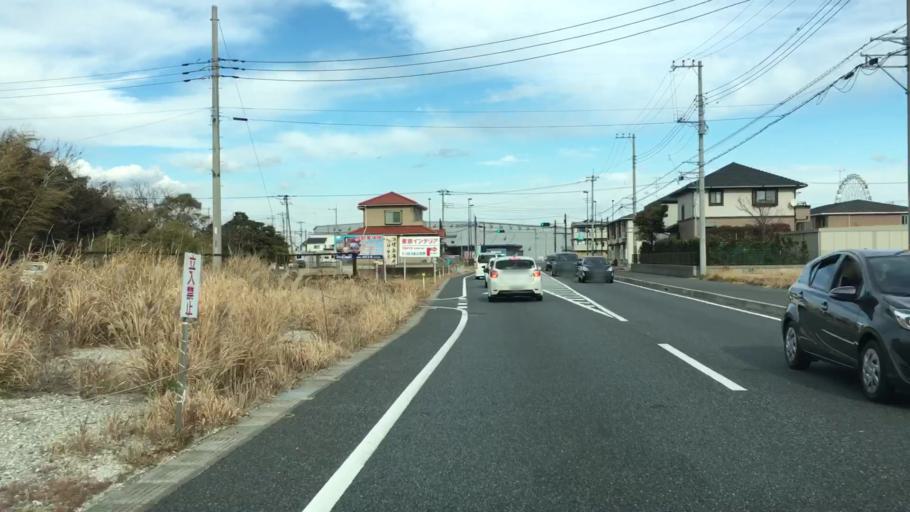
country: JP
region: Chiba
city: Kisarazu
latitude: 35.4365
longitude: 139.9255
